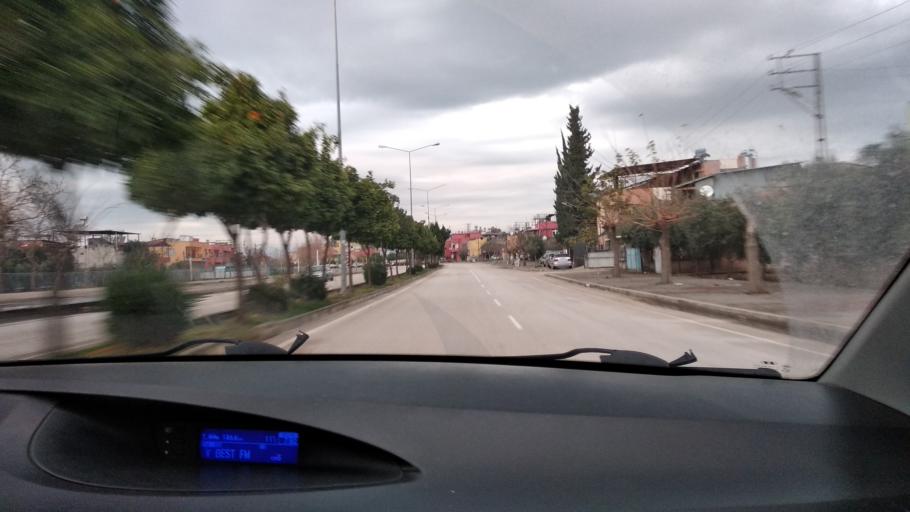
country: TR
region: Adana
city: Yuregir
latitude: 37.0130
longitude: 35.3873
